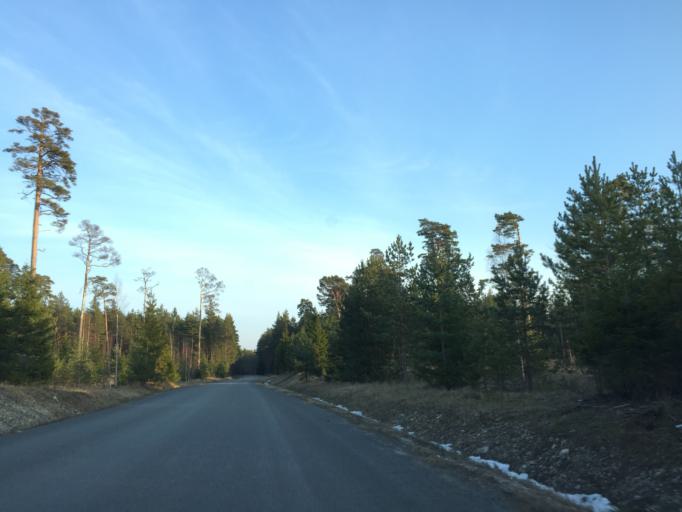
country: EE
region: Laeaene
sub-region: Lihula vald
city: Lihula
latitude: 58.4710
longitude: 23.7125
